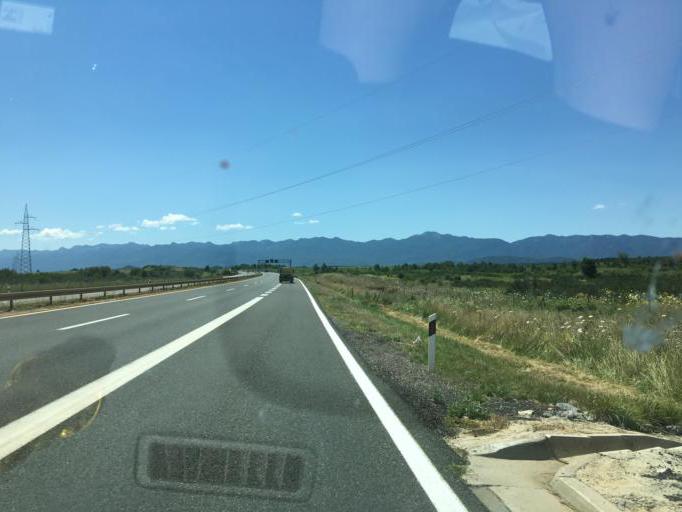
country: HR
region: Licko-Senjska
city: Gospic
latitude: 44.5715
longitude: 15.4265
